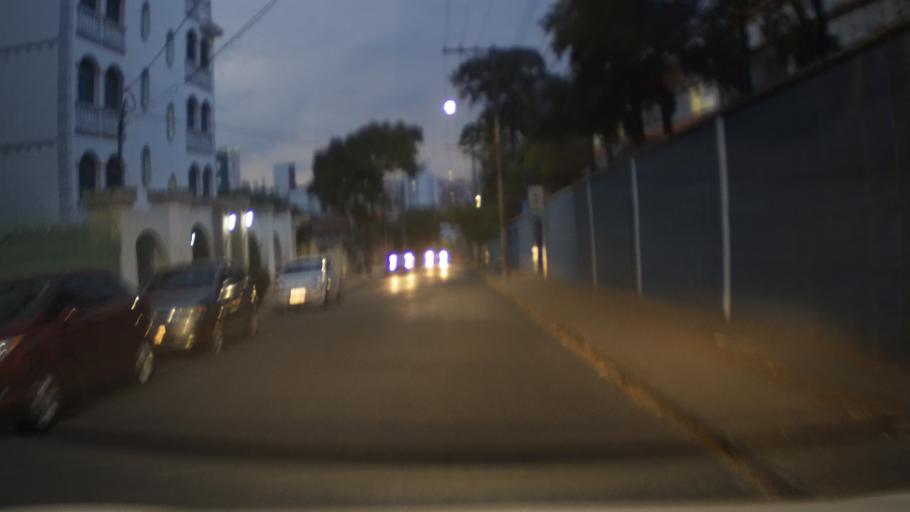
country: BR
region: Minas Gerais
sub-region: Belo Horizonte
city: Belo Horizonte
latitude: -19.8963
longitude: -43.9312
